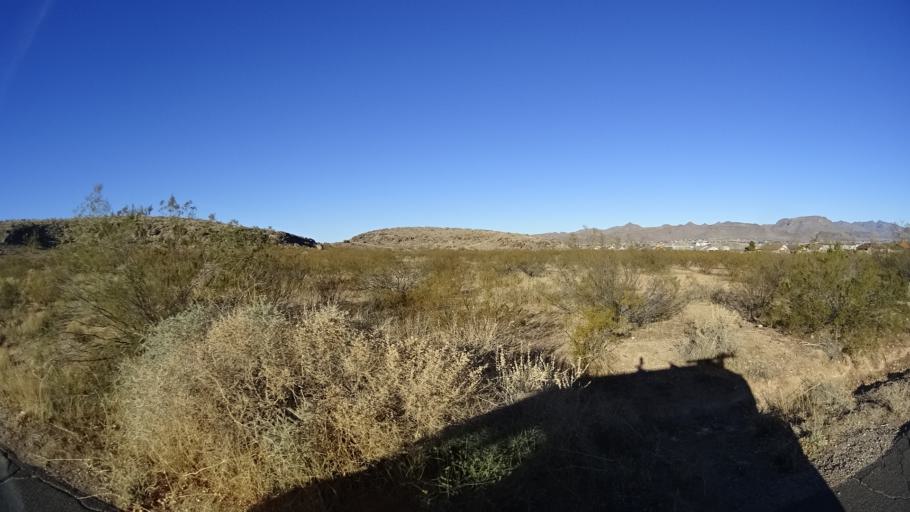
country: US
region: Arizona
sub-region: Mohave County
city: Kingman
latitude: 35.2093
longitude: -114.0023
